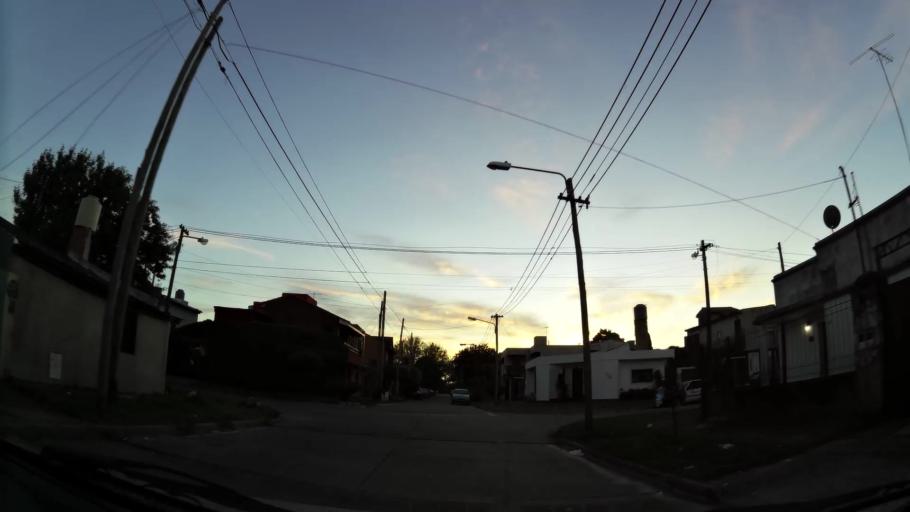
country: AR
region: Buenos Aires
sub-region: Partido de Quilmes
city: Quilmes
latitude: -34.7722
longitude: -58.1981
